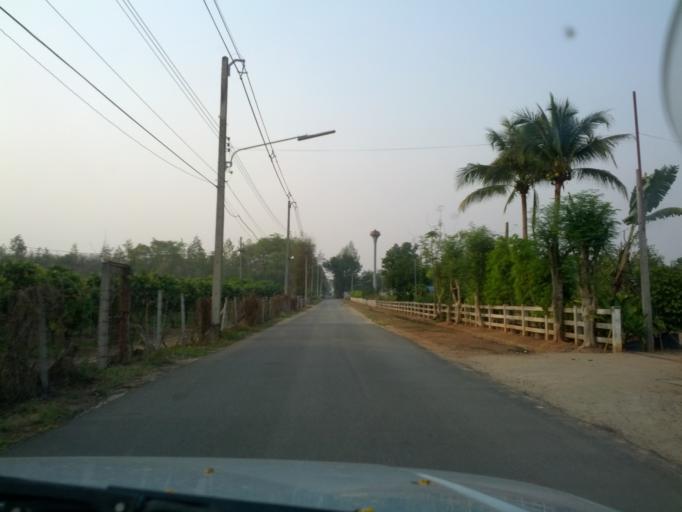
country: TH
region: Chiang Mai
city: San Sai
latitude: 18.9253
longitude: 99.0121
